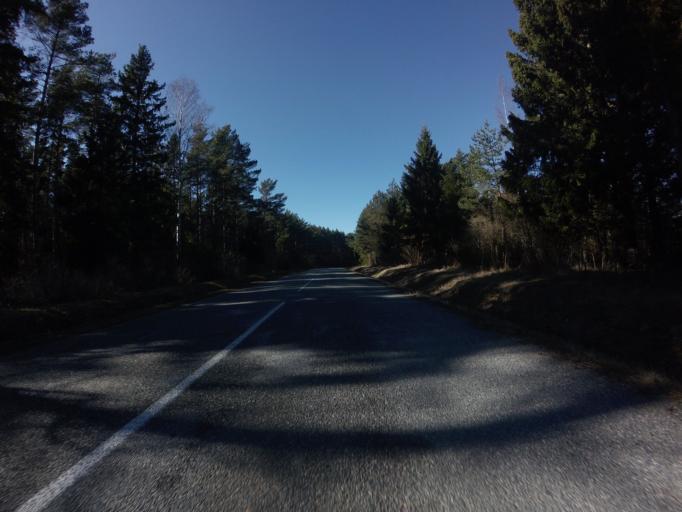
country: EE
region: Saare
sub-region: Kuressaare linn
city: Kuressaare
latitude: 58.5740
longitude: 22.4608
